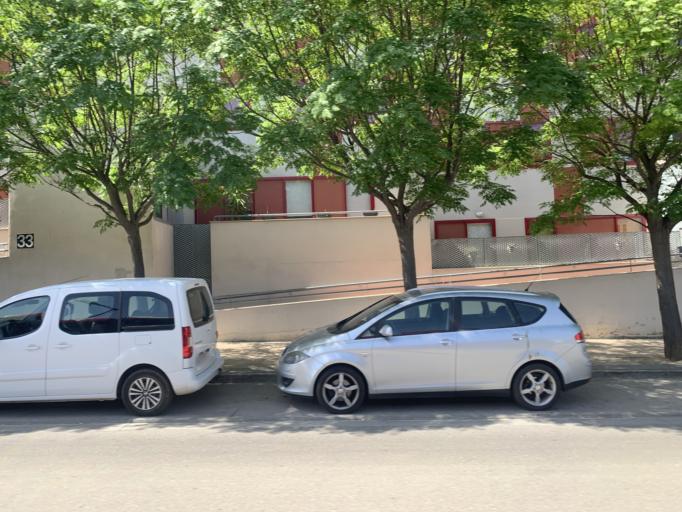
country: ES
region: Aragon
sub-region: Provincia de Zaragoza
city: Montecanal
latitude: 41.6230
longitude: -0.9310
